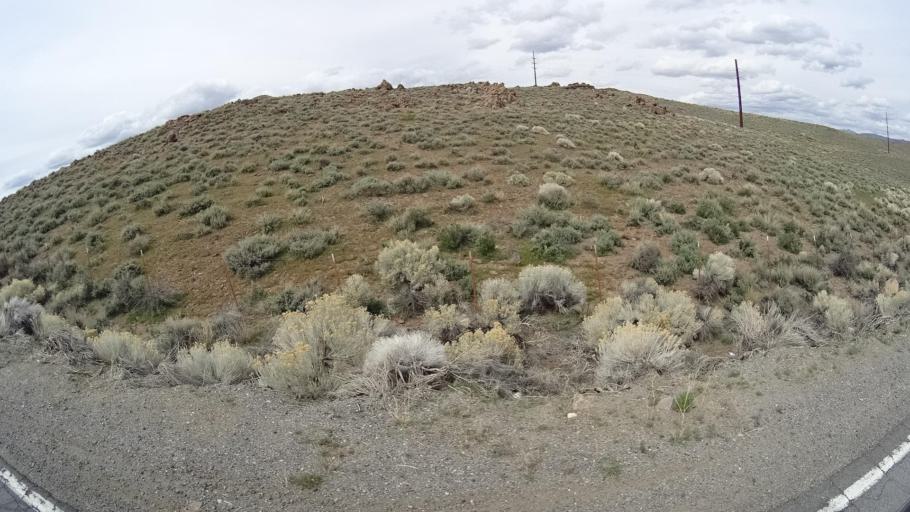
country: US
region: Nevada
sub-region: Washoe County
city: Sparks
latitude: 39.4667
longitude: -119.7516
